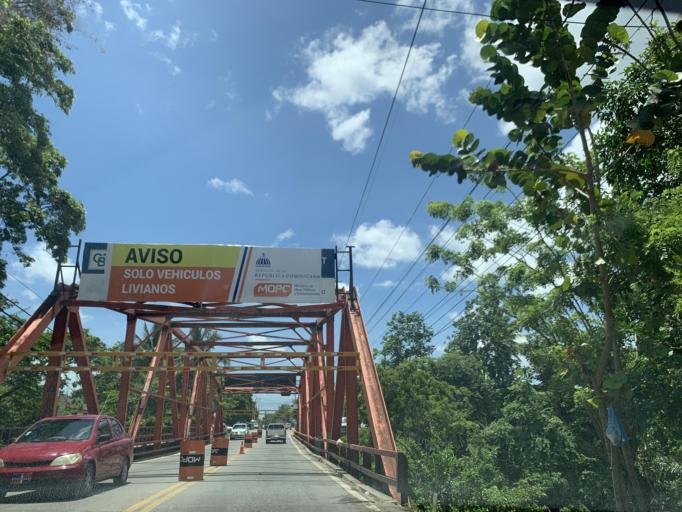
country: DO
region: Puerto Plata
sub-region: Puerto Plata
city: Puerto Plata
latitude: 19.7479
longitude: -70.5923
